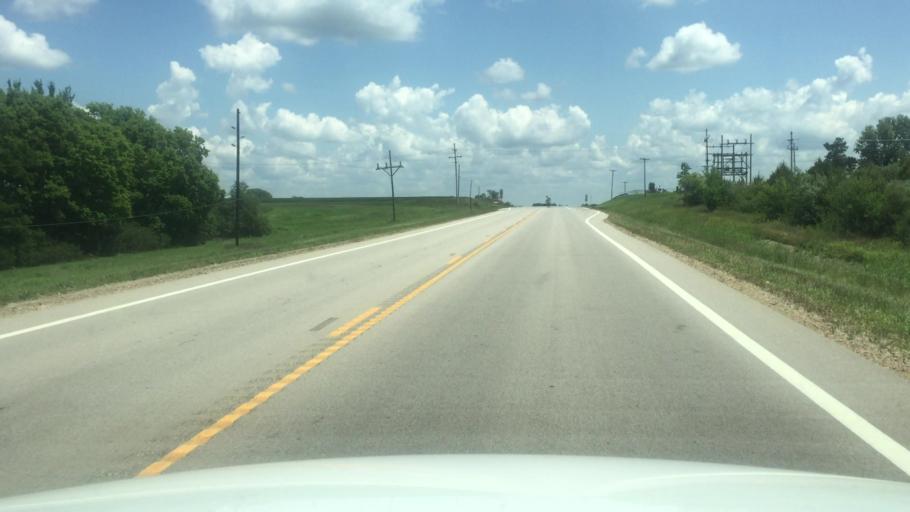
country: US
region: Kansas
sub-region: Brown County
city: Horton
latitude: 39.6675
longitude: -95.4923
